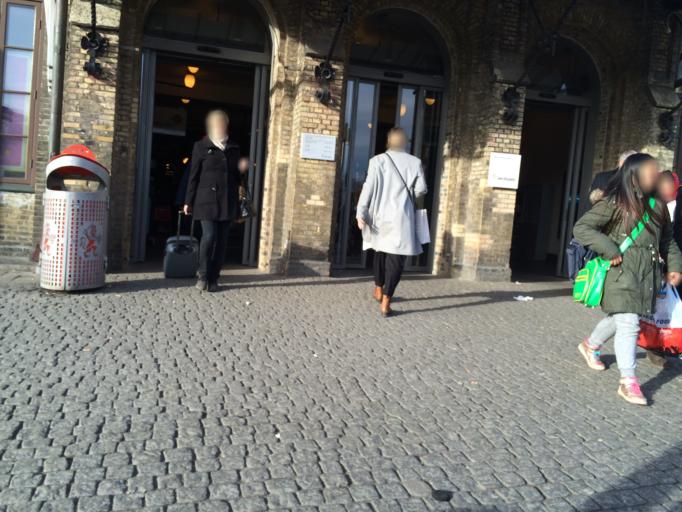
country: SE
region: Vaestra Goetaland
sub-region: Goteborg
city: Goeteborg
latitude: 57.7084
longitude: 11.9733
